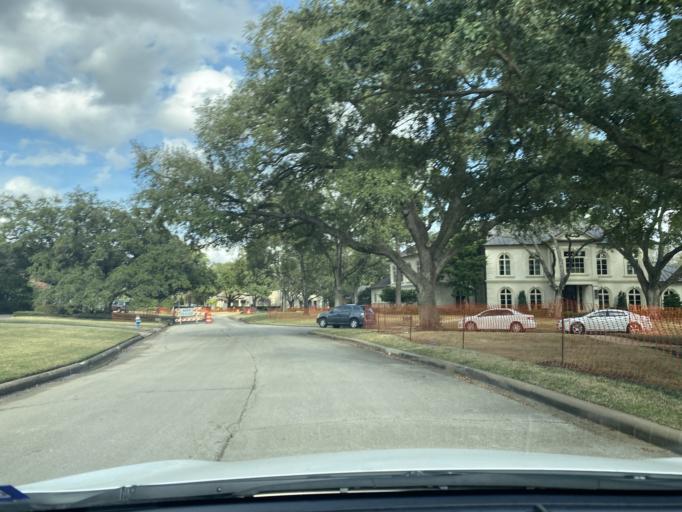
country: US
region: Texas
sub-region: Harris County
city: Hunters Creek Village
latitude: 29.7619
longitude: -95.4758
